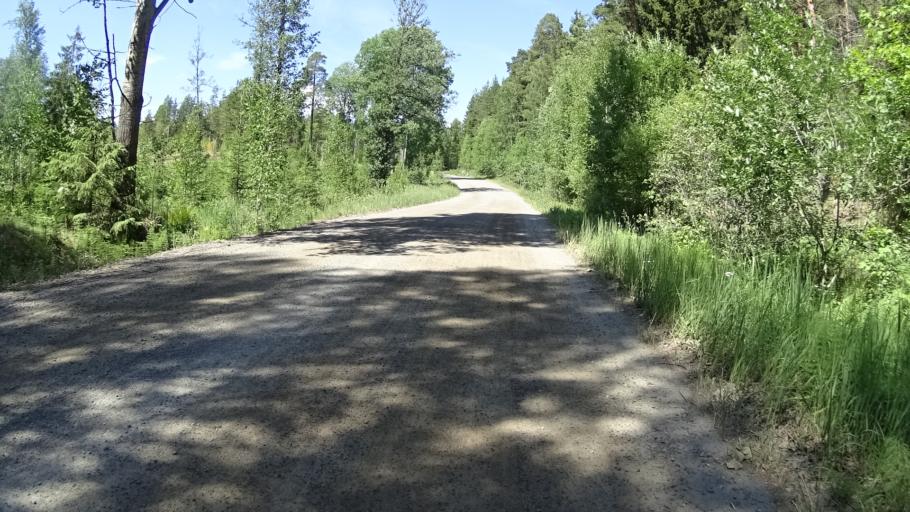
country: FI
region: Uusimaa
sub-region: Raaseporin
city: Pohja
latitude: 60.0957
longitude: 23.5636
